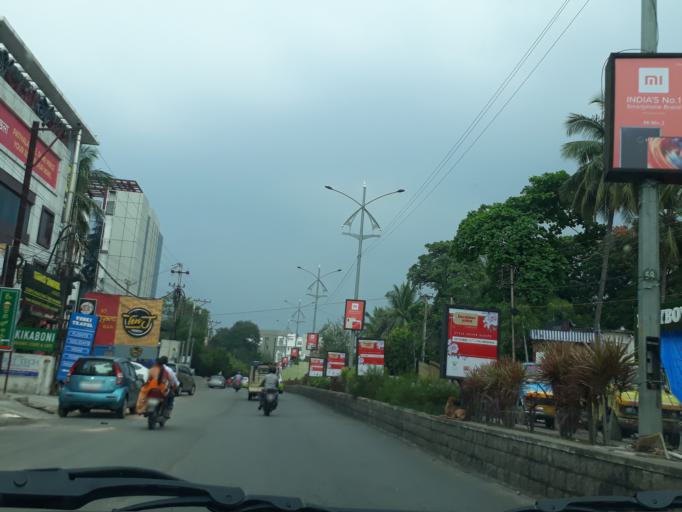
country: IN
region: Telangana
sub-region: Rangareddi
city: Kukatpalli
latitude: 17.4348
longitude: 78.4140
